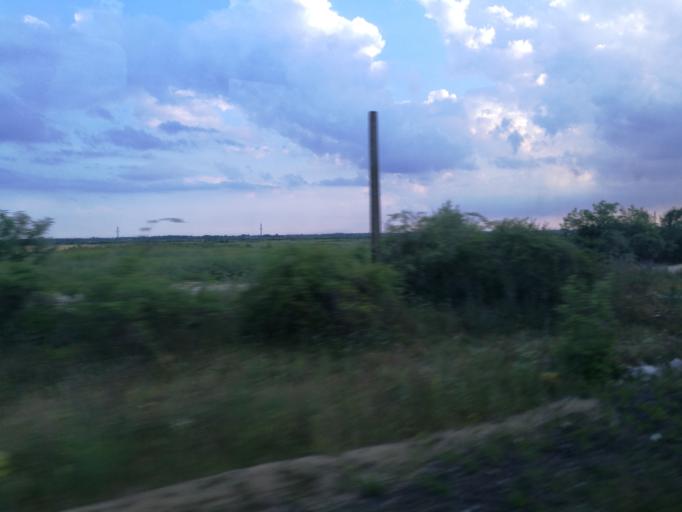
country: RO
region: Dambovita
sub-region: Comuna Produlesti
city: Costestii din Deal
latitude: 44.6751
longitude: 25.4965
